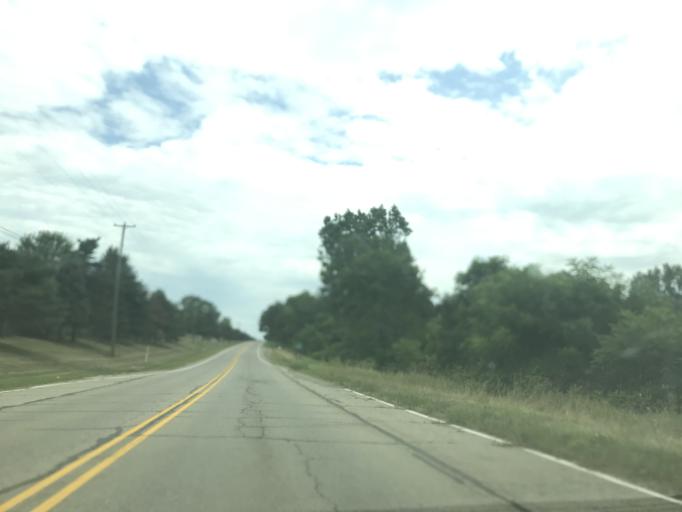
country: US
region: Michigan
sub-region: Clinton County
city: Wacousta
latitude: 42.7895
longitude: -84.6930
